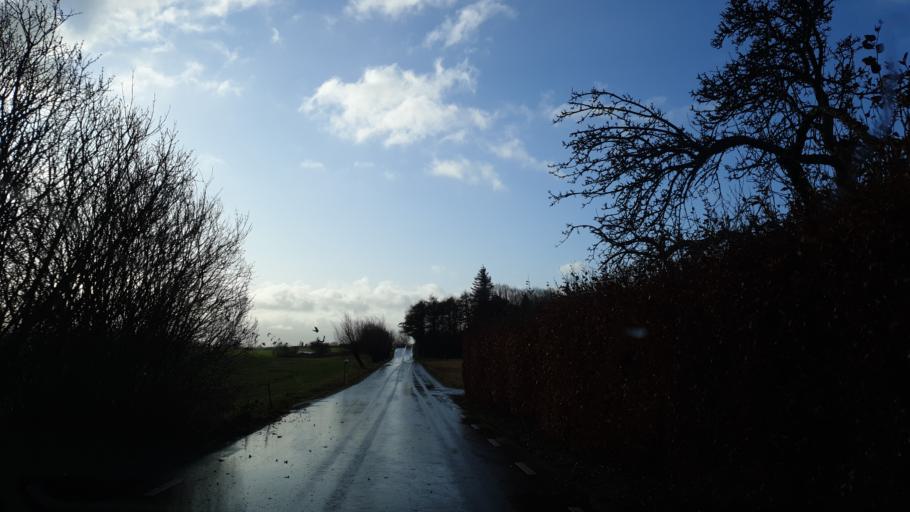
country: SE
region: Skane
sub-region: Skurups Kommun
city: Rydsgard
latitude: 55.4593
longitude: 13.5562
